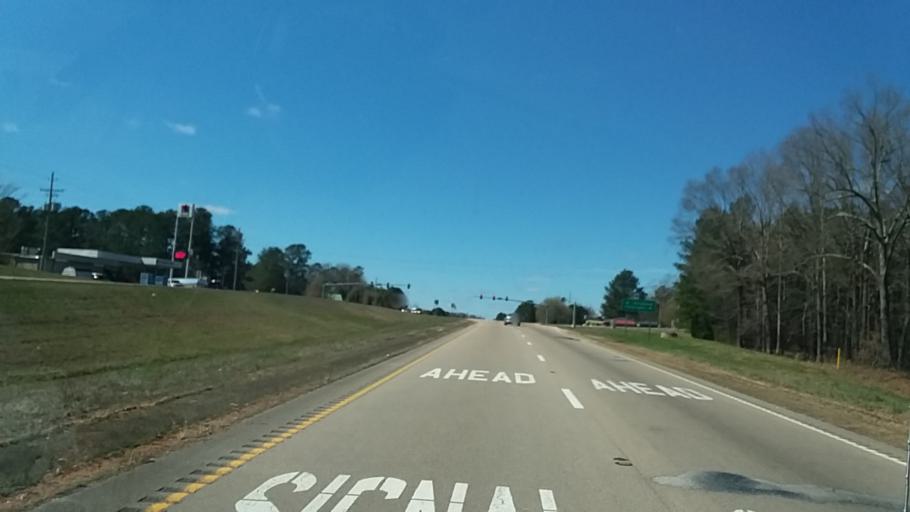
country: US
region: Mississippi
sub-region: Alcorn County
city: Farmington
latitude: 34.8777
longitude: -88.4392
